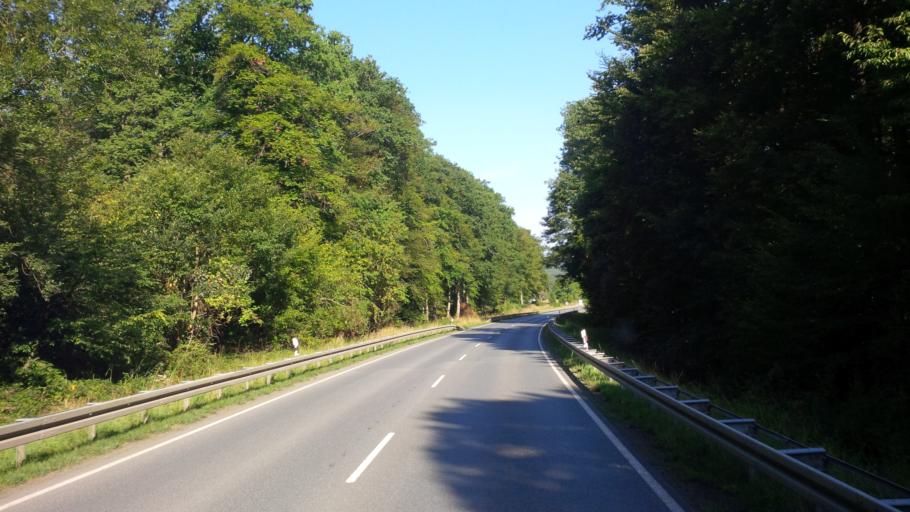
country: DE
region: Hesse
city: Weilmunster
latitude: 50.4464
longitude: 8.3976
